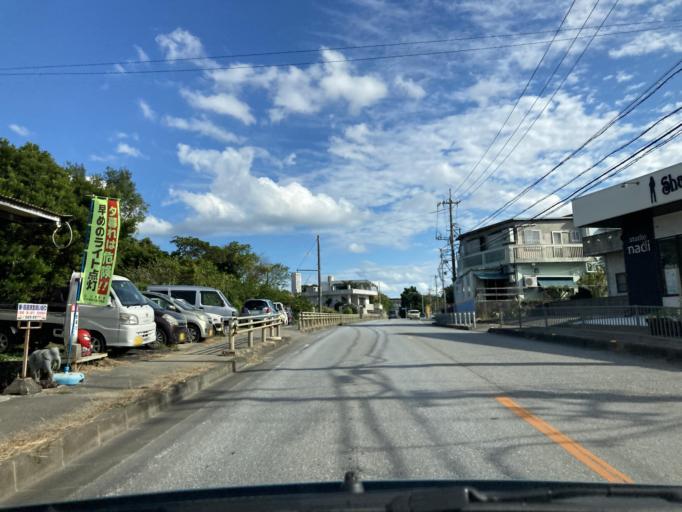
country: JP
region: Okinawa
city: Ishikawa
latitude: 26.4214
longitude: 127.8123
